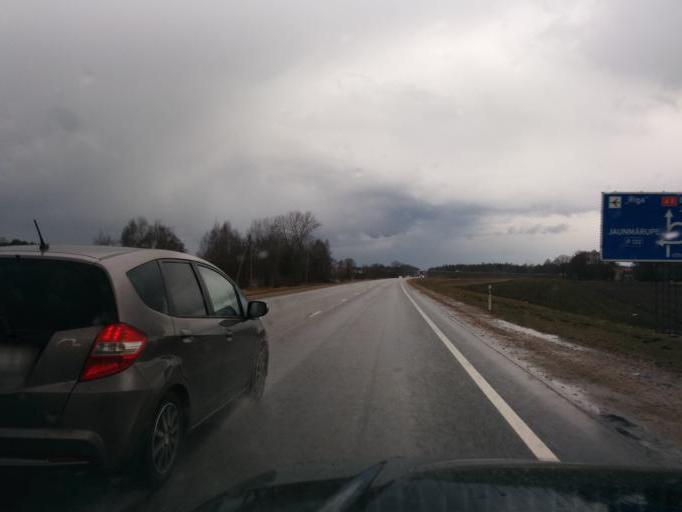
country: LV
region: Babite
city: Pinki
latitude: 56.8733
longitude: 23.9599
